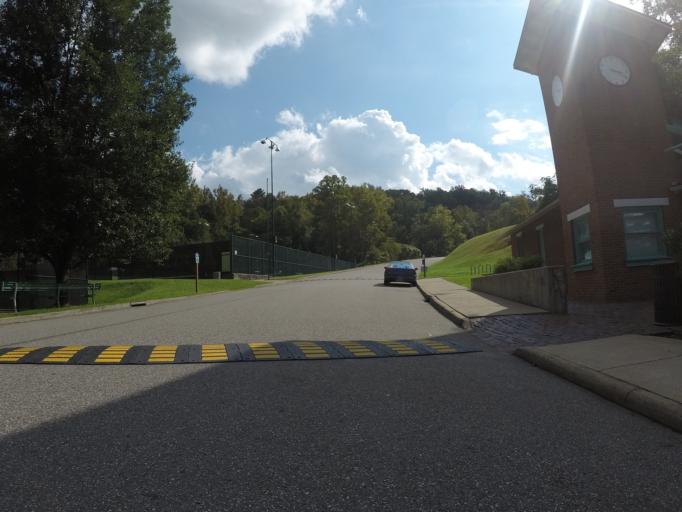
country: US
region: West Virginia
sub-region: Cabell County
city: Huntington
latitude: 38.4063
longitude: -82.4344
